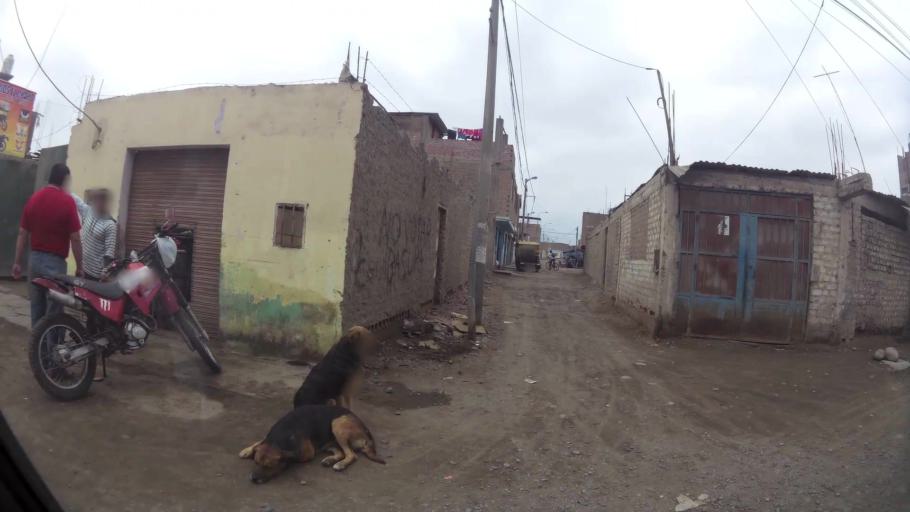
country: PE
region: Lima
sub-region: Provincia de Huaral
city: Huaral
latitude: -11.4895
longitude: -77.2094
